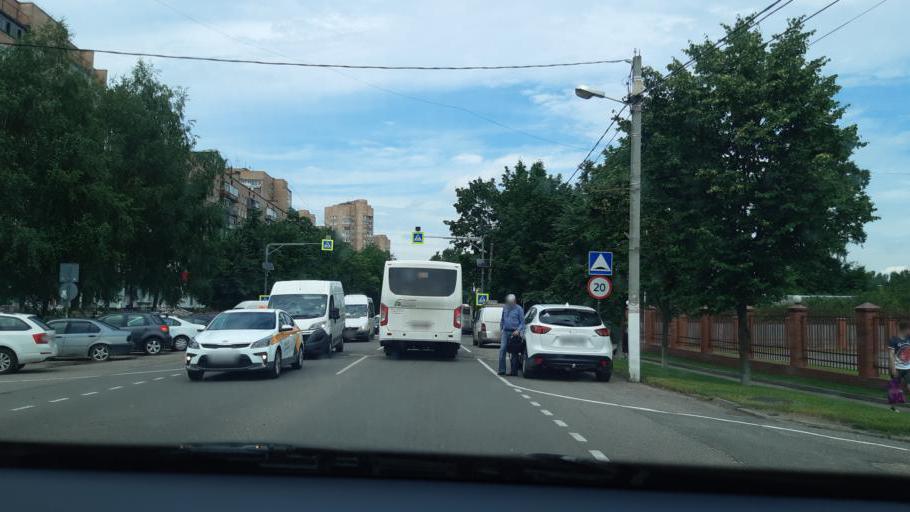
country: RU
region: Moskovskaya
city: Bol'shiye Vyazemy
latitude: 55.6200
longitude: 36.9851
